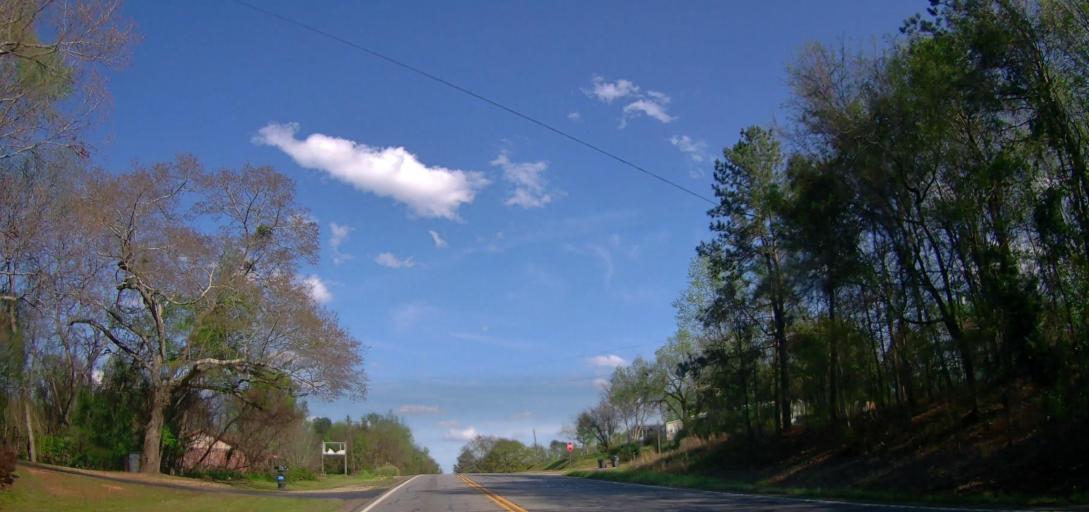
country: US
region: Georgia
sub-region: Baldwin County
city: Hardwick
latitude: 33.0917
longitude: -83.1828
